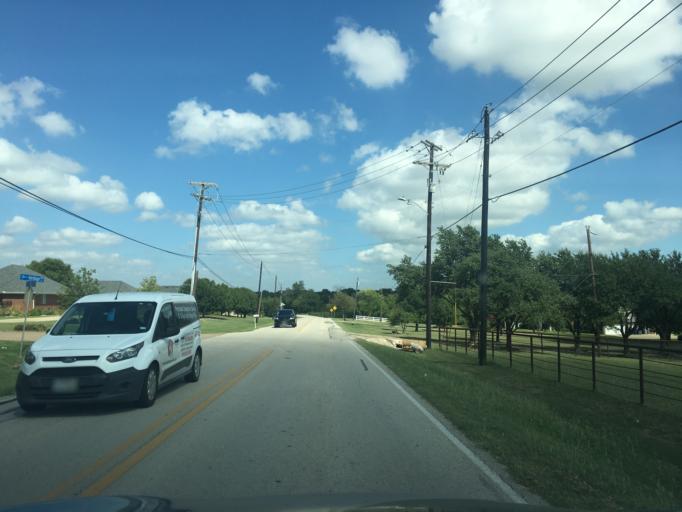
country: US
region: Texas
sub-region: Dallas County
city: Sachse
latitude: 32.9696
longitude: -96.5703
